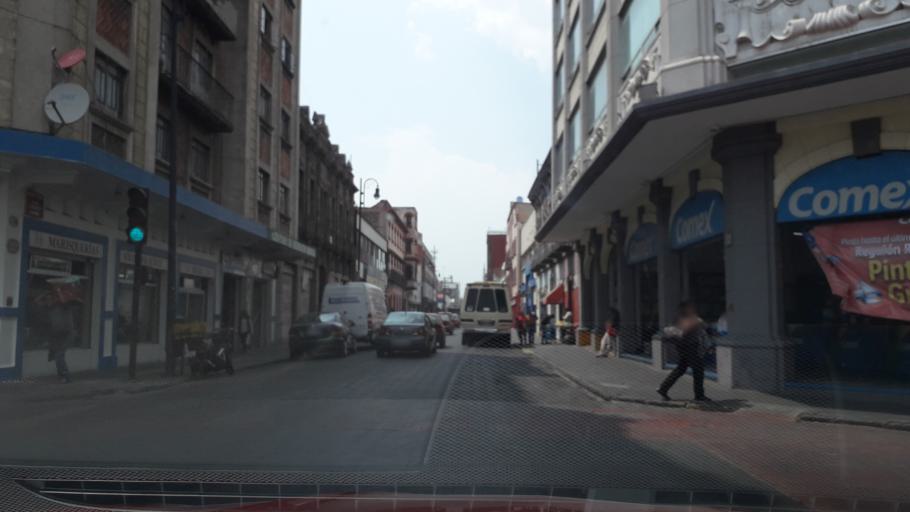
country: MX
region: Puebla
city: Puebla
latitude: 19.0483
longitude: -98.2042
